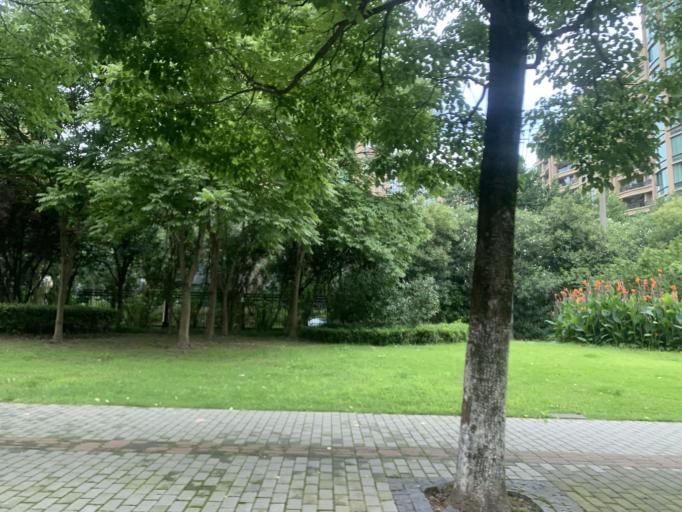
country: CN
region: Shanghai Shi
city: Huamu
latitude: 31.2072
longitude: 121.5316
